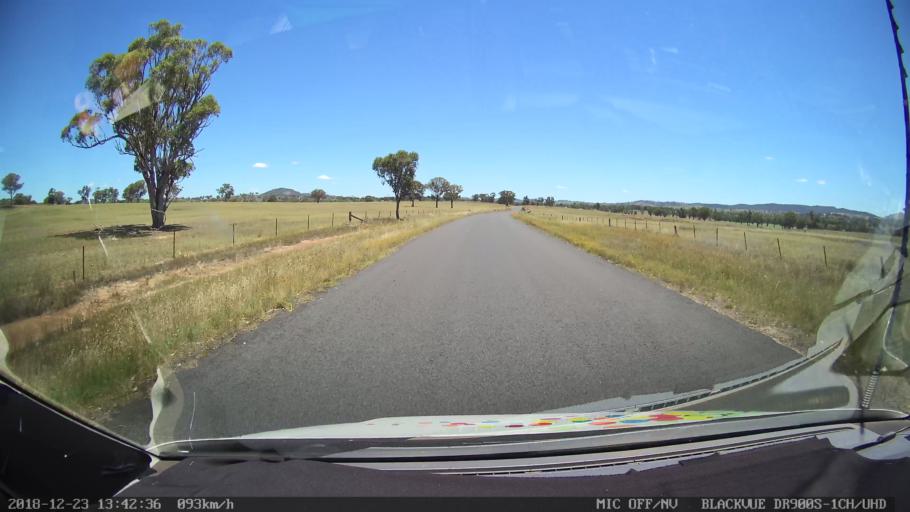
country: AU
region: New South Wales
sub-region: Armidale Dumaresq
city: Armidale
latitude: -30.4788
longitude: 151.1609
